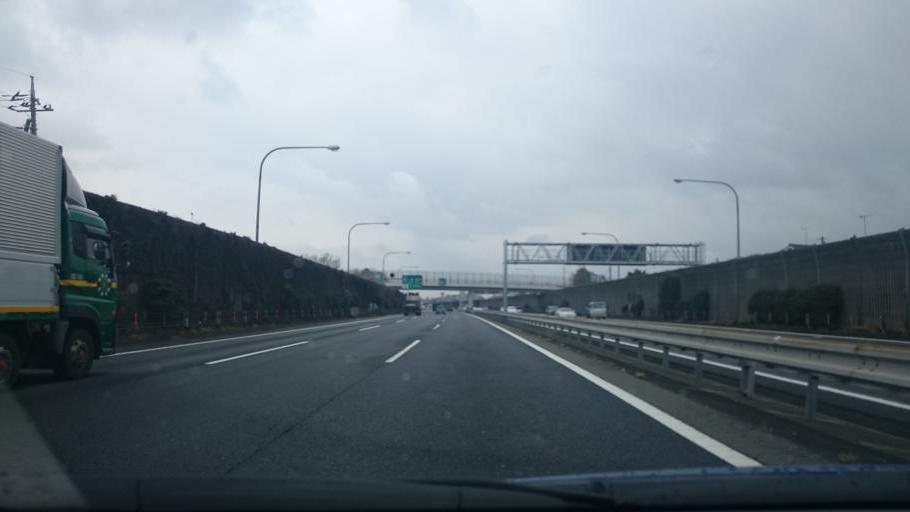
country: JP
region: Saitama
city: Sakado
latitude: 35.9392
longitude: 139.4039
